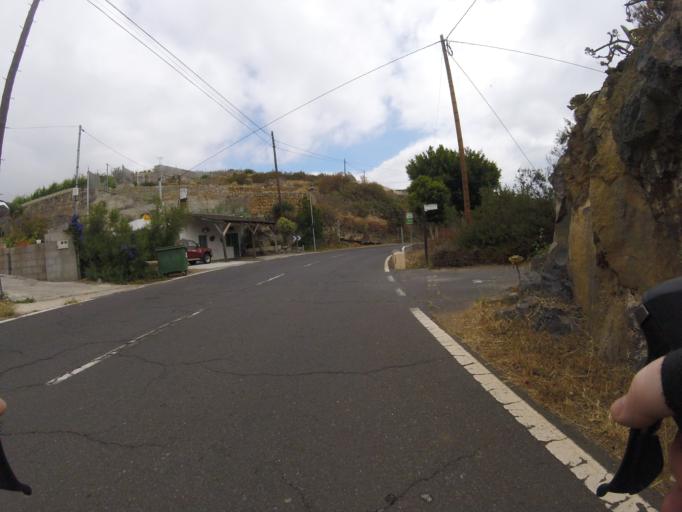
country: ES
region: Canary Islands
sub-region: Provincia de Santa Cruz de Tenerife
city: Guimar
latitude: 28.2834
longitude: -16.4074
